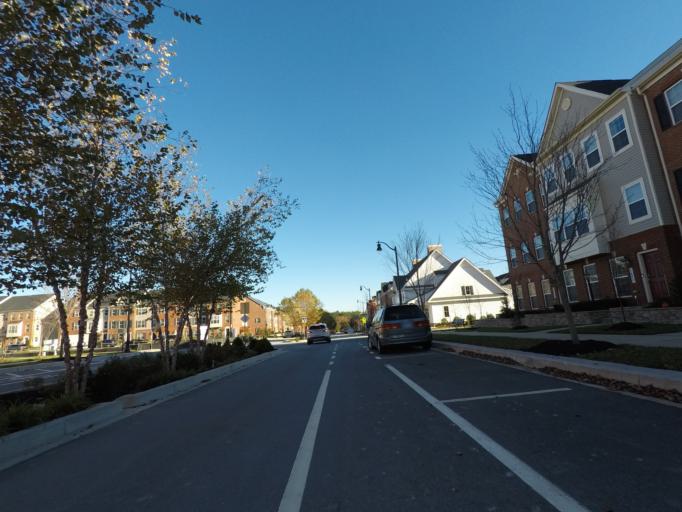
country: US
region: Maryland
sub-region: Howard County
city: Hanover
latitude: 39.1837
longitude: -76.7394
